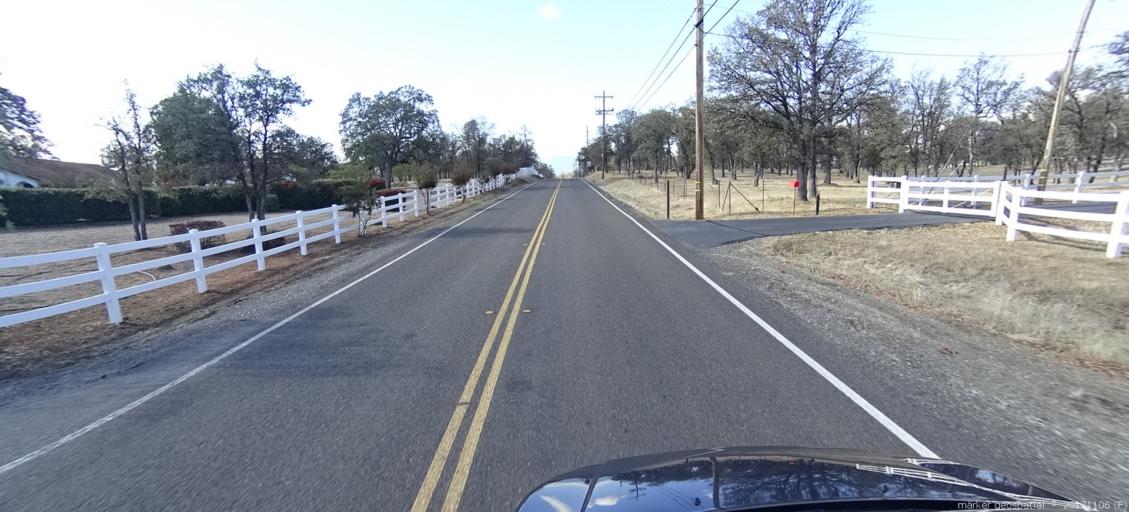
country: US
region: California
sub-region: Shasta County
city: Palo Cedro
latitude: 40.5928
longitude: -122.2603
